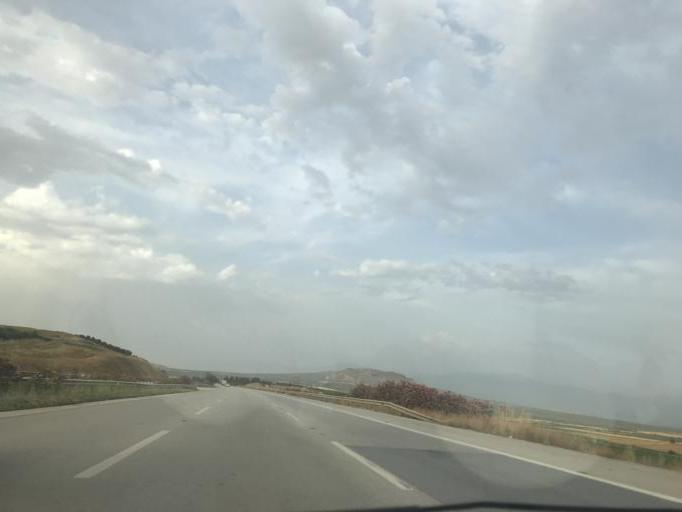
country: TR
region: Adana
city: Kosreli
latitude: 37.0149
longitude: 35.9980
